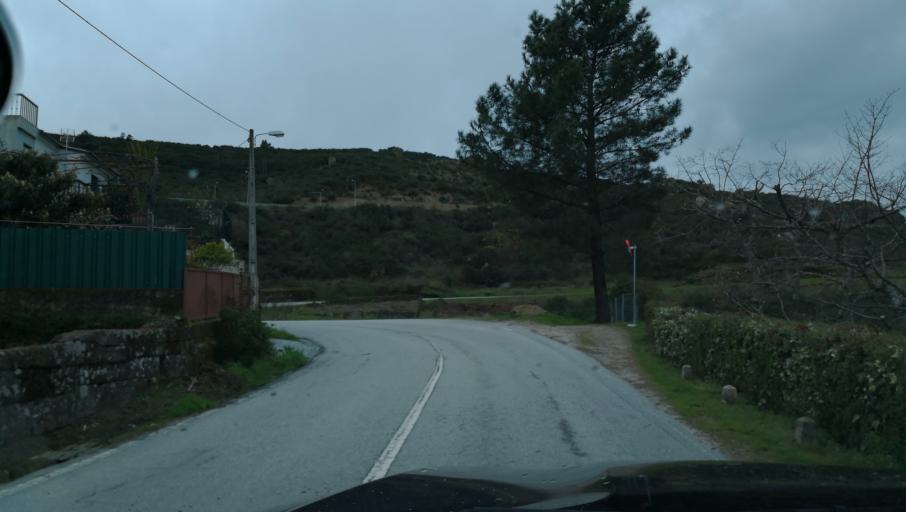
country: PT
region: Vila Real
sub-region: Vila Real
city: Vila Real
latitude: 41.2770
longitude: -7.7812
